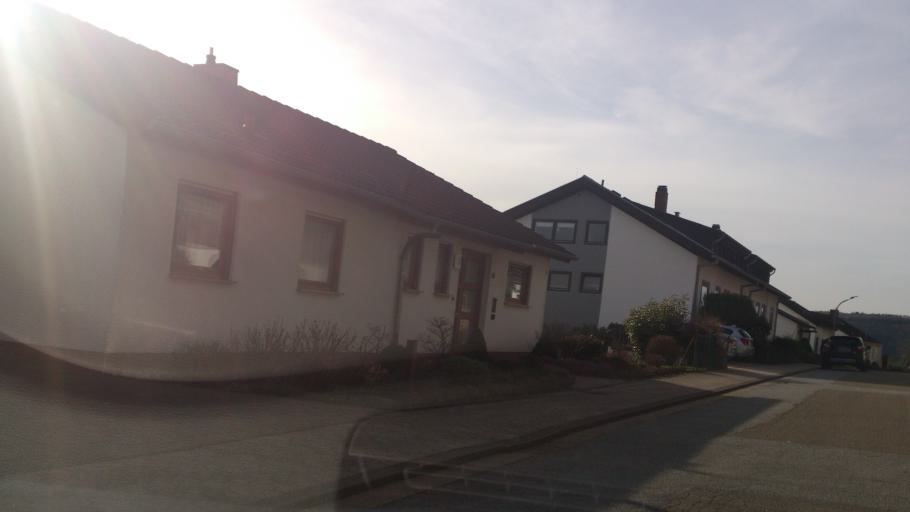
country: DE
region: Rheinland-Pfalz
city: Zweibrucken
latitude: 49.2670
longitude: 7.3271
